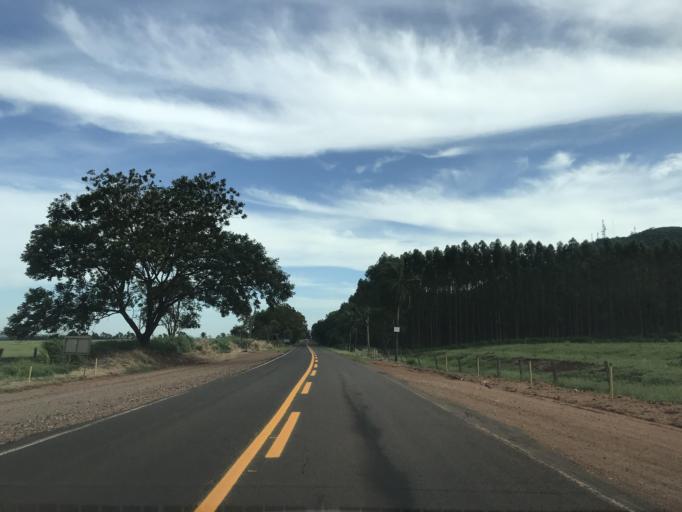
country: BR
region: Parana
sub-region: Terra Rica
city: Terra Rica
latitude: -22.7941
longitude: -52.6529
